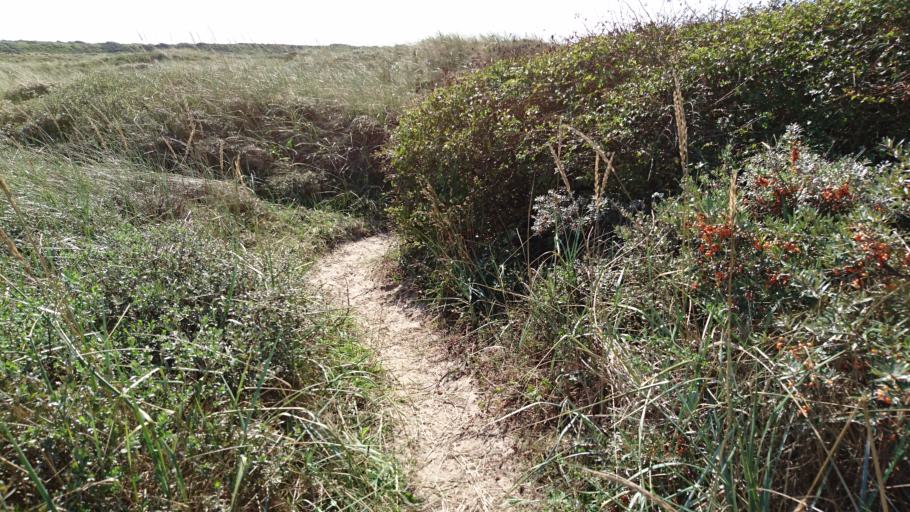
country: DK
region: North Denmark
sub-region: Hjorring Kommune
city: Hirtshals
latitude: 57.5173
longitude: 9.8699
